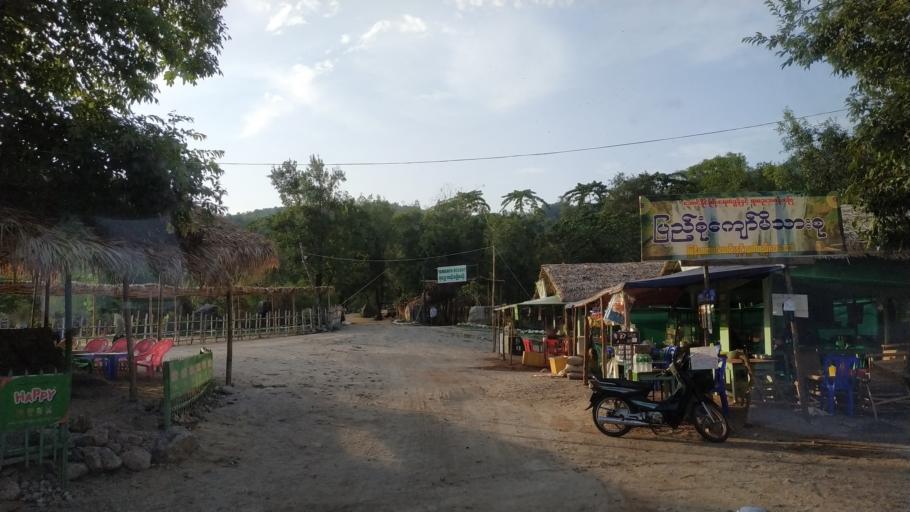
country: MM
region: Mon
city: Kyaikto
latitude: 17.4369
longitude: 97.0396
